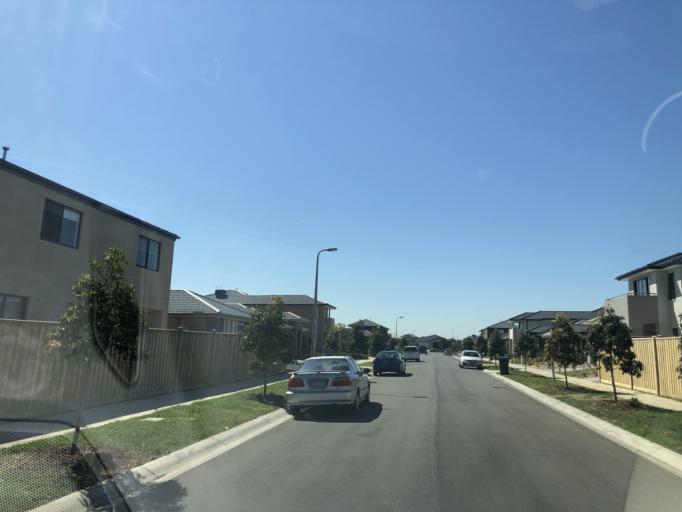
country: AU
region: Victoria
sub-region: Wyndham
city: Hoppers Crossing
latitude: -37.9062
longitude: 144.7186
